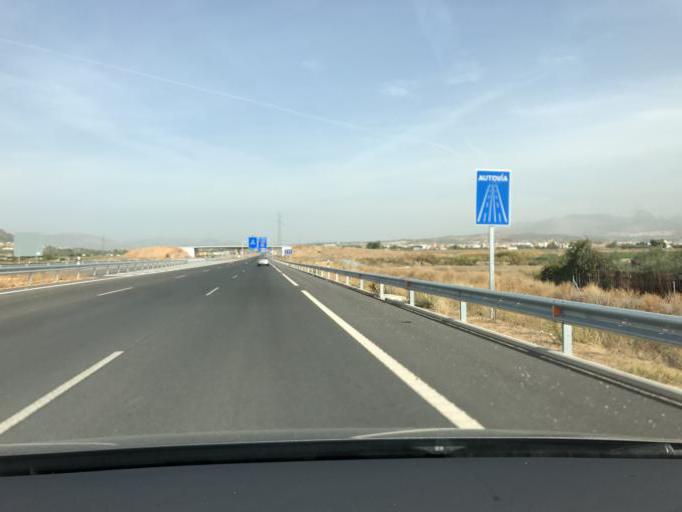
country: ES
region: Andalusia
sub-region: Provincia de Granada
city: Atarfe
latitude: 37.2138
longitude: -3.6723
